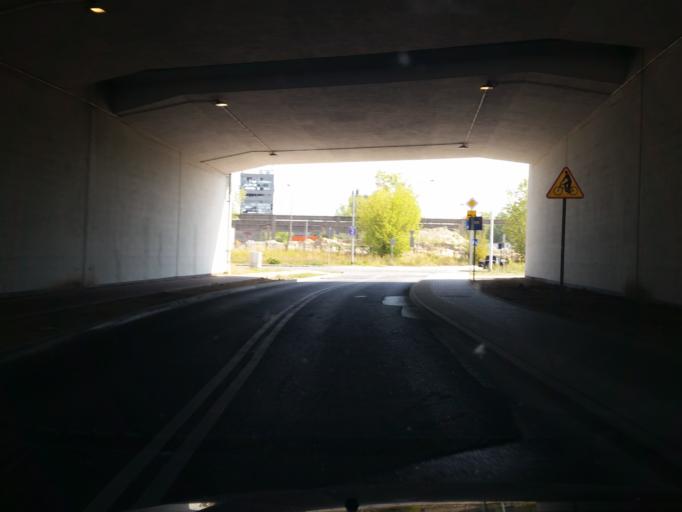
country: PL
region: Masovian Voivodeship
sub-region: Warszawa
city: Bialoleka
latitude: 52.3110
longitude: 20.9603
